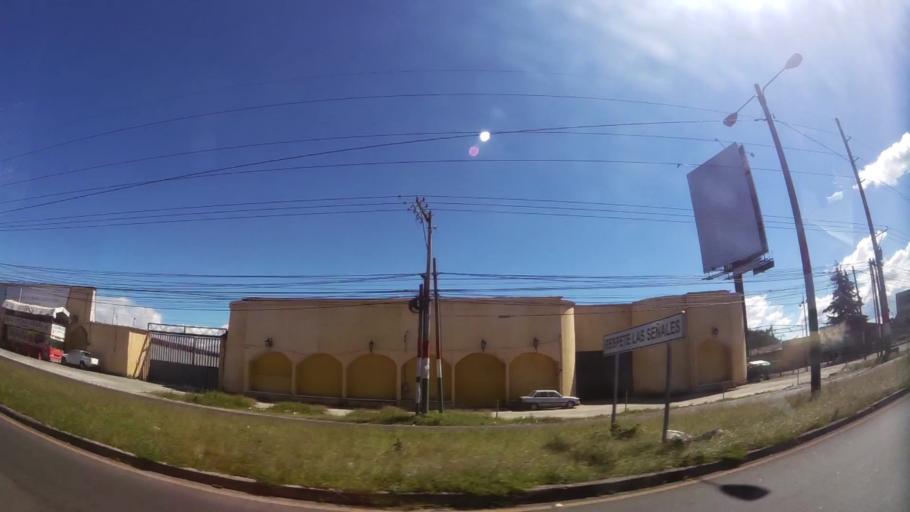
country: GT
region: Guatemala
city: Fraijanes
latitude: 14.5124
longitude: -90.4764
